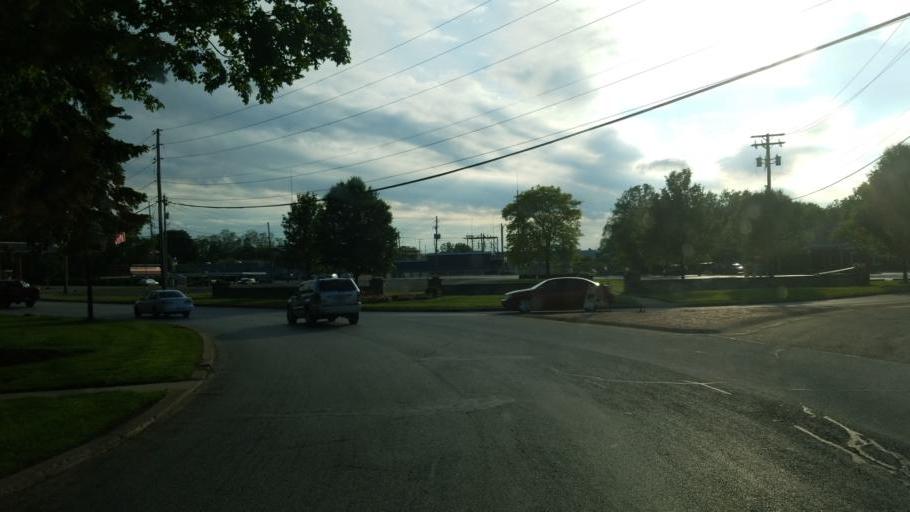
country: US
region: Ohio
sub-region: Summit County
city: Tallmadge
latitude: 41.1020
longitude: -81.4417
